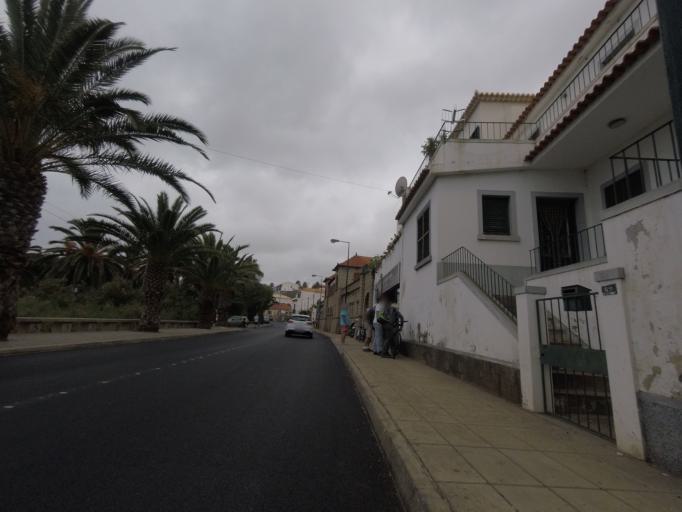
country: PT
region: Madeira
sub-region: Porto Santo
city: Vila de Porto Santo
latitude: 33.0576
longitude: -16.3381
